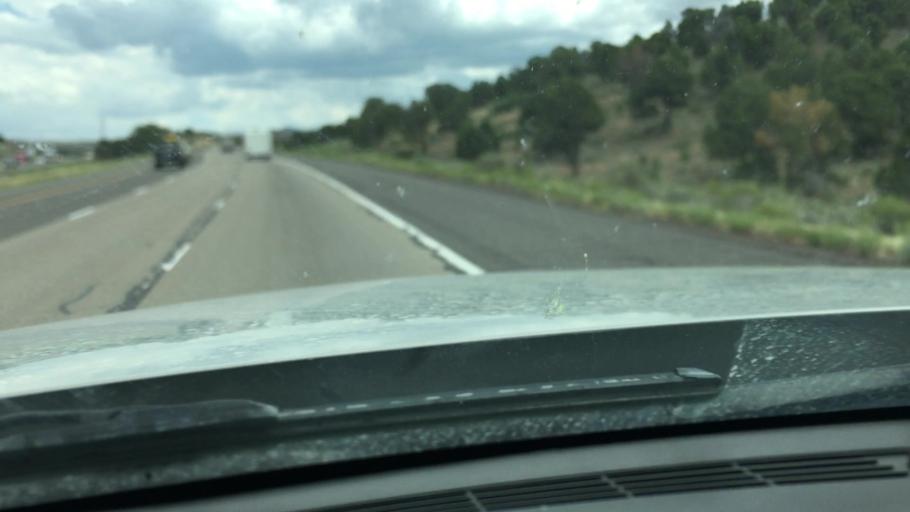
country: US
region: Utah
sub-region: Beaver County
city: Beaver
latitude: 38.1627
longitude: -112.6195
